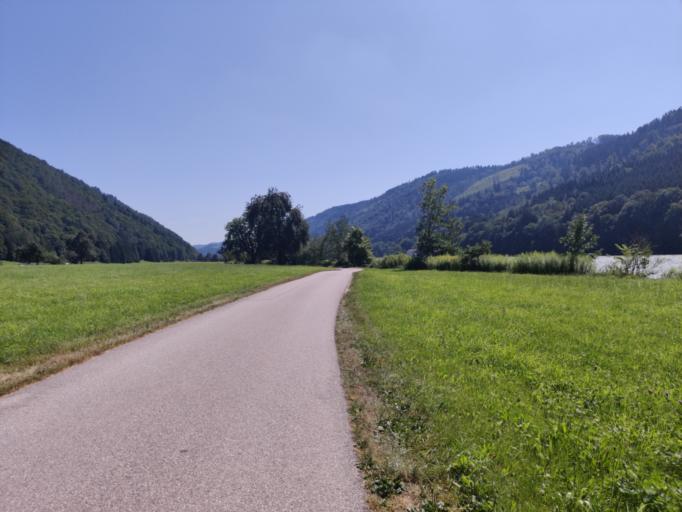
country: AT
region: Upper Austria
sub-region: Politischer Bezirk Rohrbach
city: Pfarrkirchen im Muehlkreis
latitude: 48.4478
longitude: 13.8301
